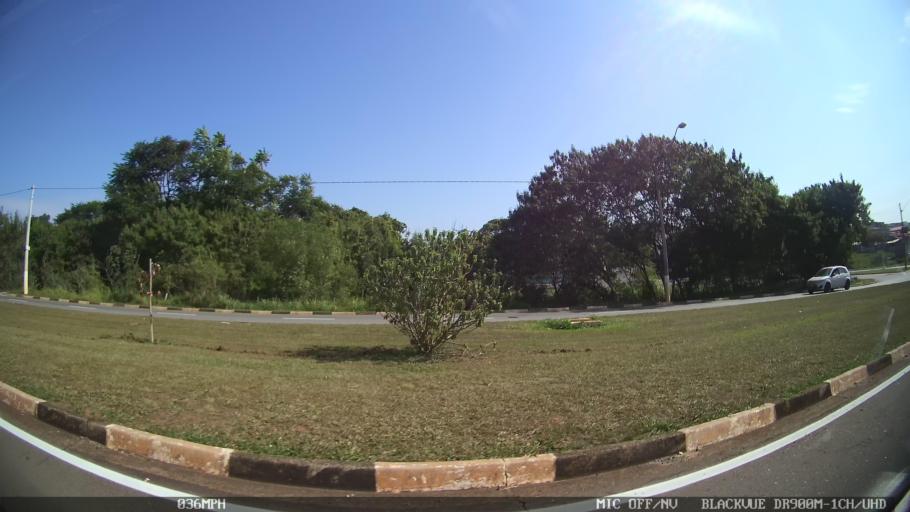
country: BR
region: Sao Paulo
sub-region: Paulinia
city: Paulinia
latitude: -22.7791
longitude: -47.1646
